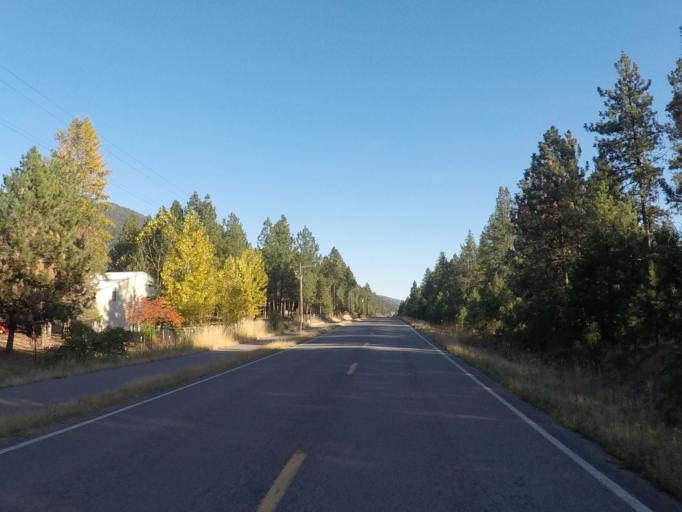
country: US
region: Montana
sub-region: Missoula County
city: Bonner-West Riverside
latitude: 46.8413
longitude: -113.8360
